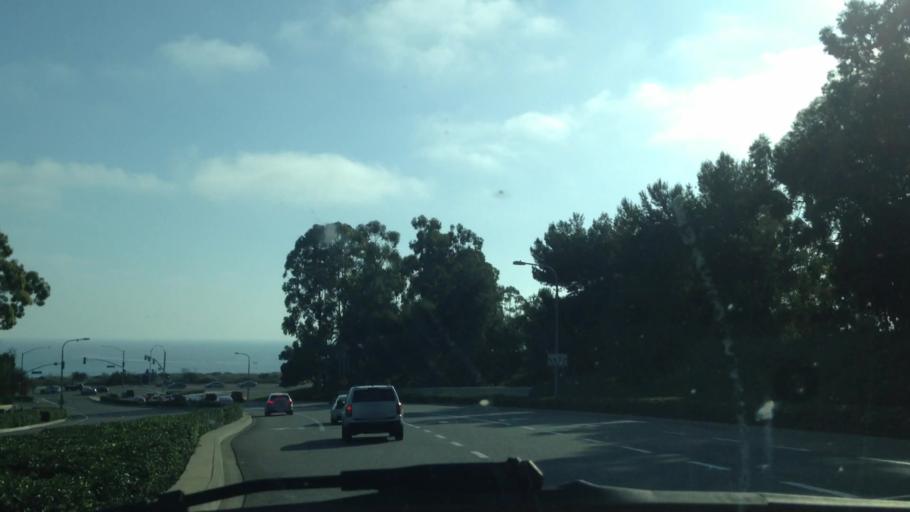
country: US
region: California
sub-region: Orange County
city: San Joaquin Hills
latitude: 33.5845
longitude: -117.8470
